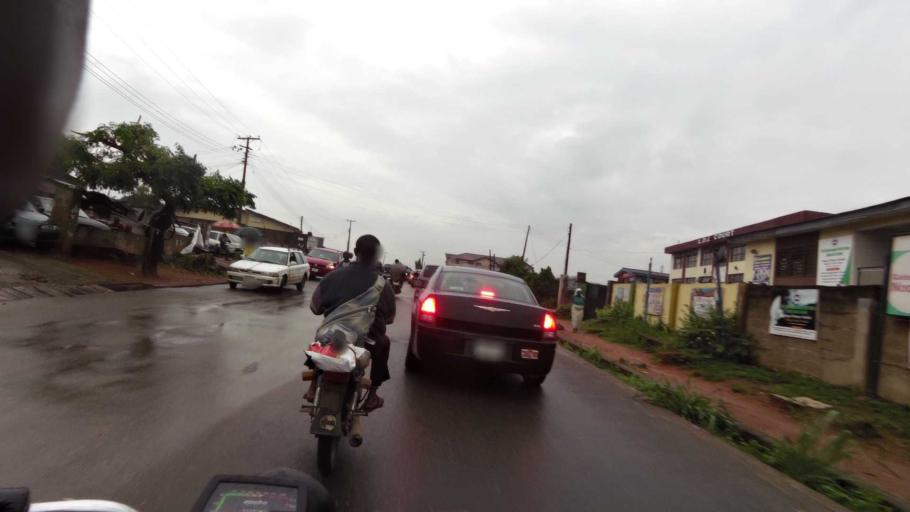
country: NG
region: Oyo
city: Ibadan
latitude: 7.4204
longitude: 3.9351
